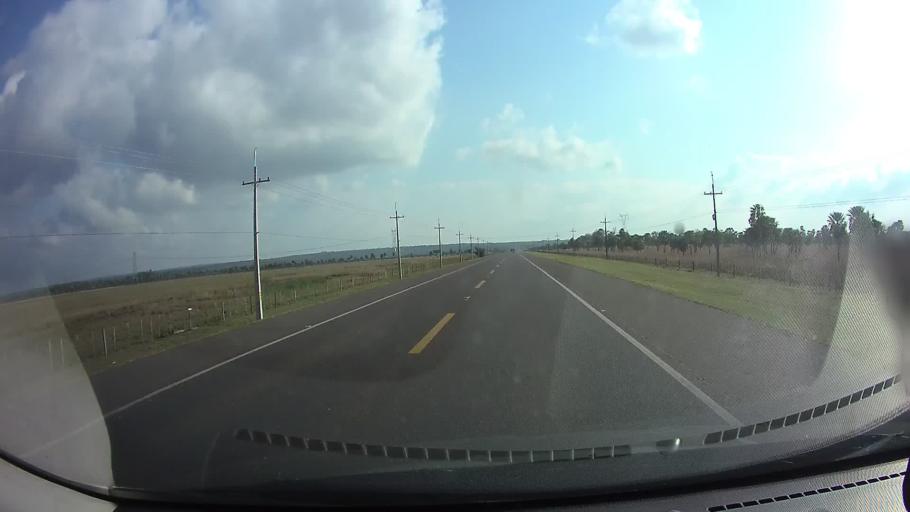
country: PY
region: Cordillera
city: Emboscada
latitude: -25.0794
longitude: -57.2735
